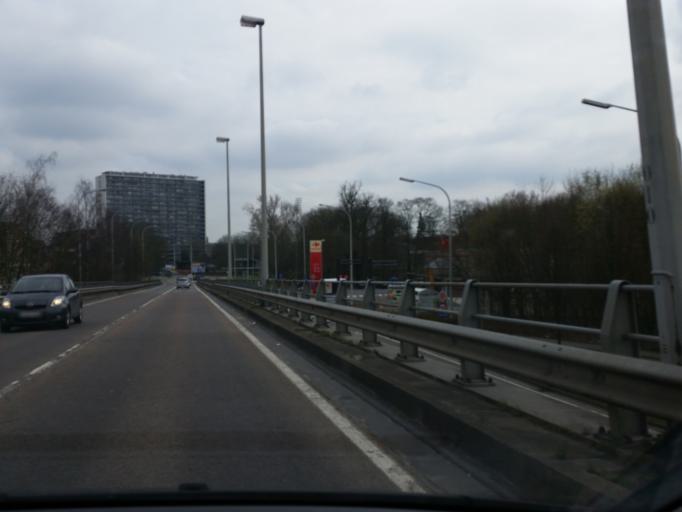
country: BE
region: Flanders
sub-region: Provincie Vlaams-Brabant
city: Leuven
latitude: 50.8717
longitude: 4.6912
